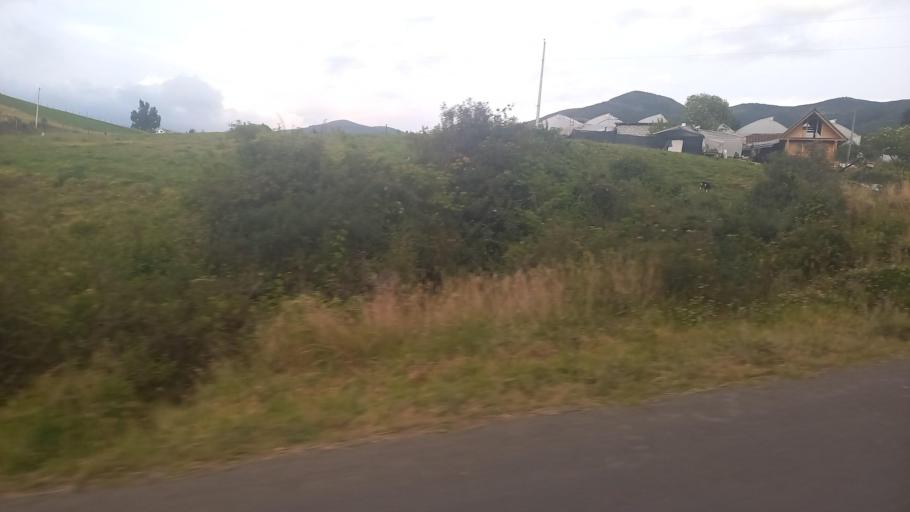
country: EC
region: Pichincha
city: Cayambe
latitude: 0.0949
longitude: -78.0909
